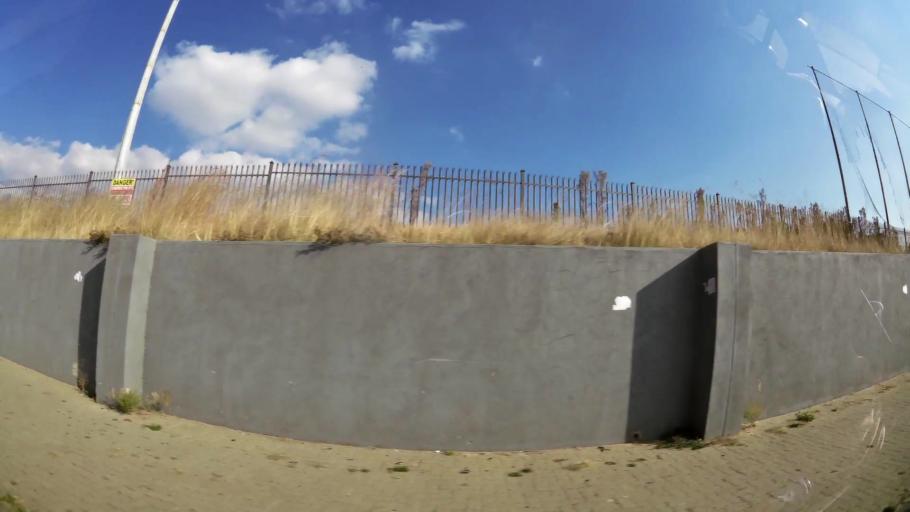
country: ZA
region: Gauteng
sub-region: West Rand District Municipality
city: Krugersdorp
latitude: -26.0998
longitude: 27.7787
